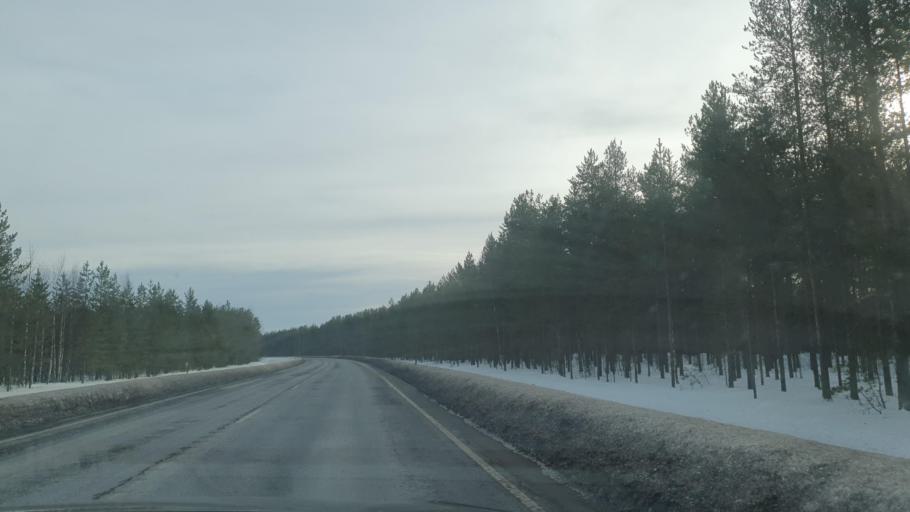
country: FI
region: Northern Ostrobothnia
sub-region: Oulunkaari
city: Utajaervi
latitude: 64.7095
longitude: 26.5162
